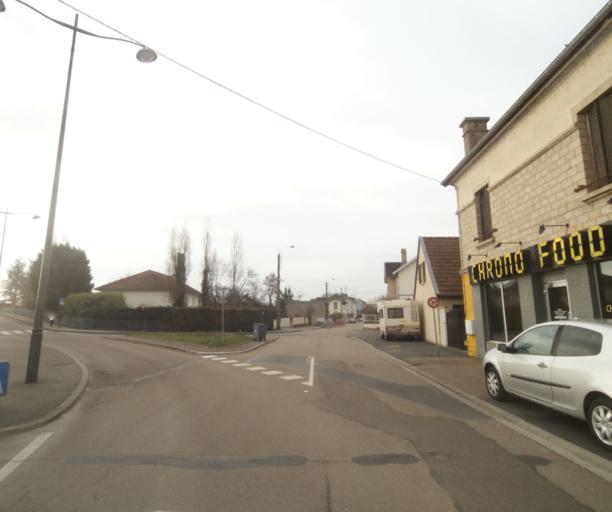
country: FR
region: Champagne-Ardenne
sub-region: Departement de la Haute-Marne
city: Bettancourt-la-Ferree
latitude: 48.6407
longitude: 4.9610
